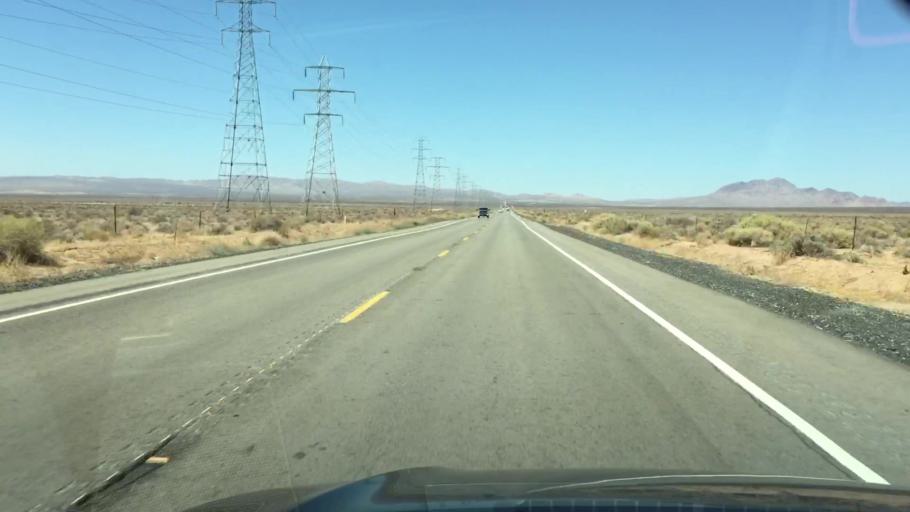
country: US
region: California
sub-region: Kern County
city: Boron
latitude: 35.1790
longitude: -117.5936
